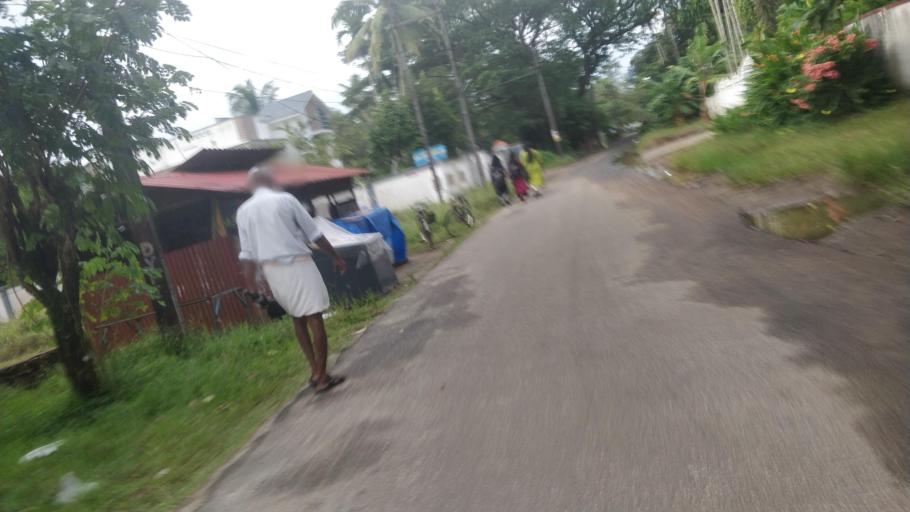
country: IN
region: Kerala
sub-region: Alappuzha
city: Vayalar
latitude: 9.7008
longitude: 76.3477
